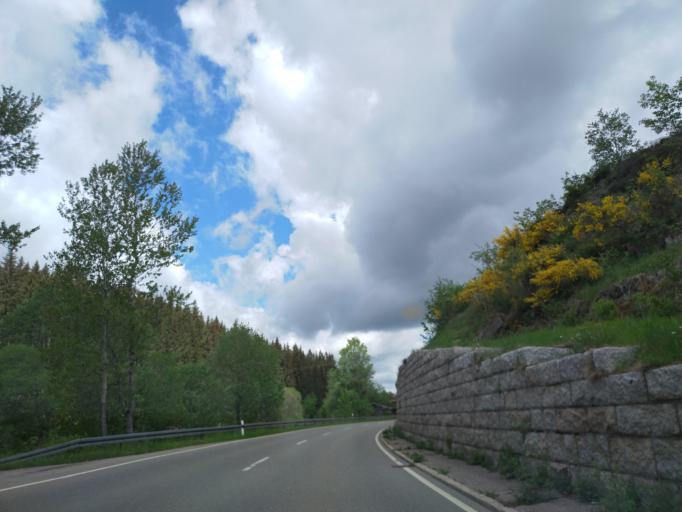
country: DE
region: Baden-Wuerttemberg
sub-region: Freiburg Region
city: Vohrenbach
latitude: 48.0328
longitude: 8.3123
